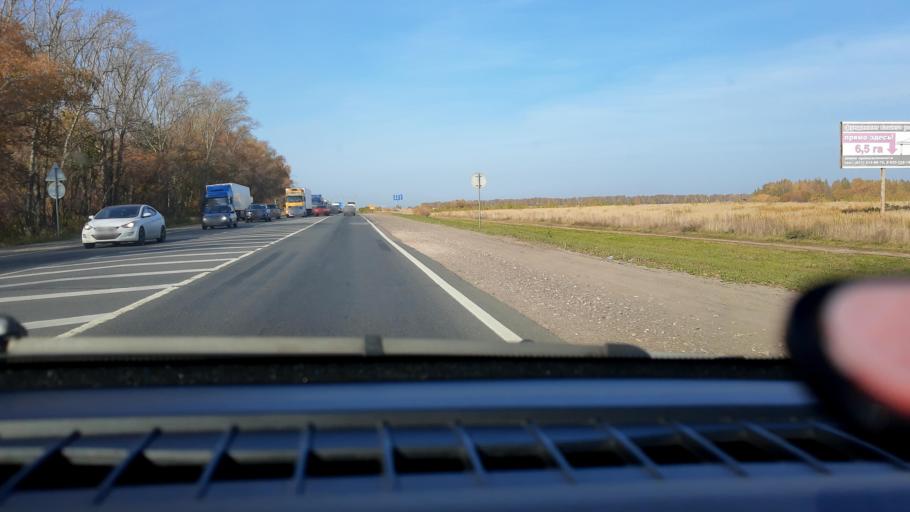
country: RU
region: Nizjnij Novgorod
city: Kstovo
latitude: 56.1204
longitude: 44.2727
